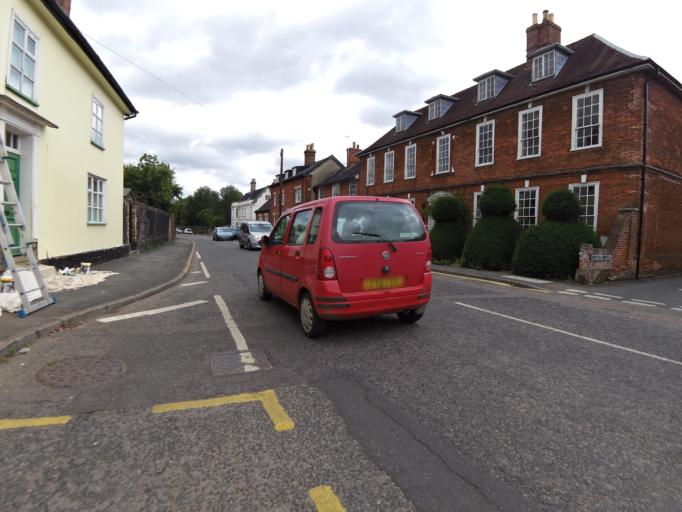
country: GB
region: England
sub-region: Norfolk
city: Harleston
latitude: 52.4043
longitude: 1.3017
